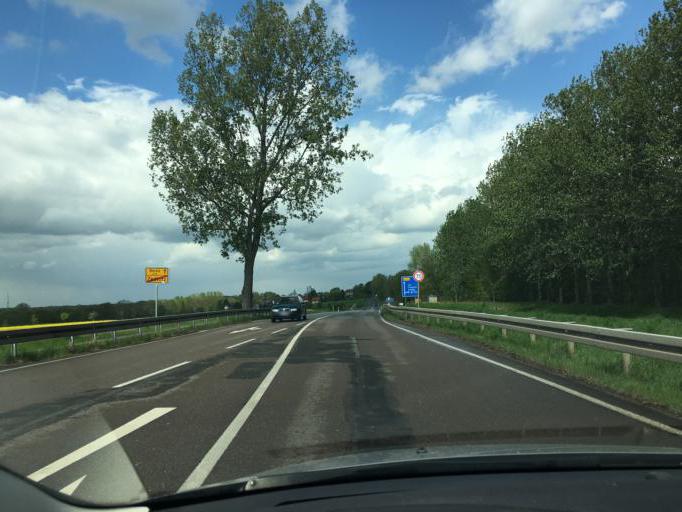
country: DE
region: Saxony
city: Borna
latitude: 51.1088
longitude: 12.5116
